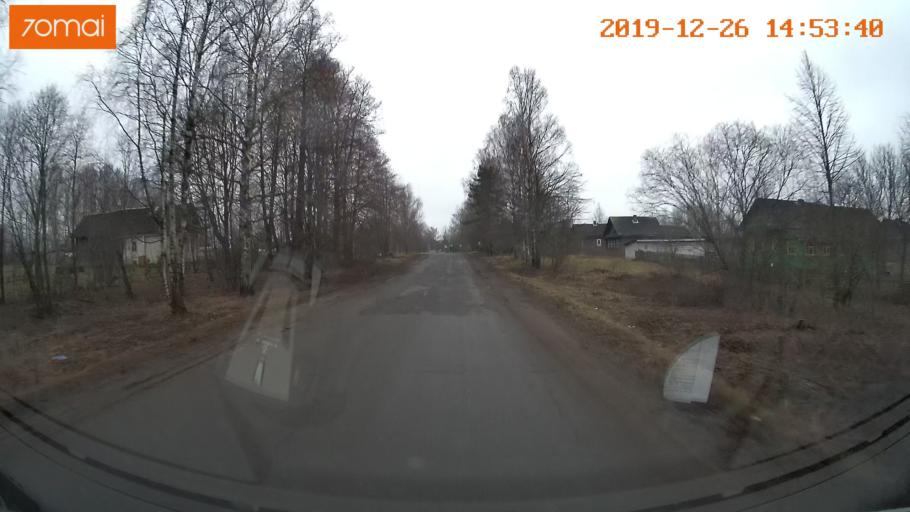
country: RU
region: Jaroslavl
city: Rybinsk
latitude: 58.3134
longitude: 38.8879
